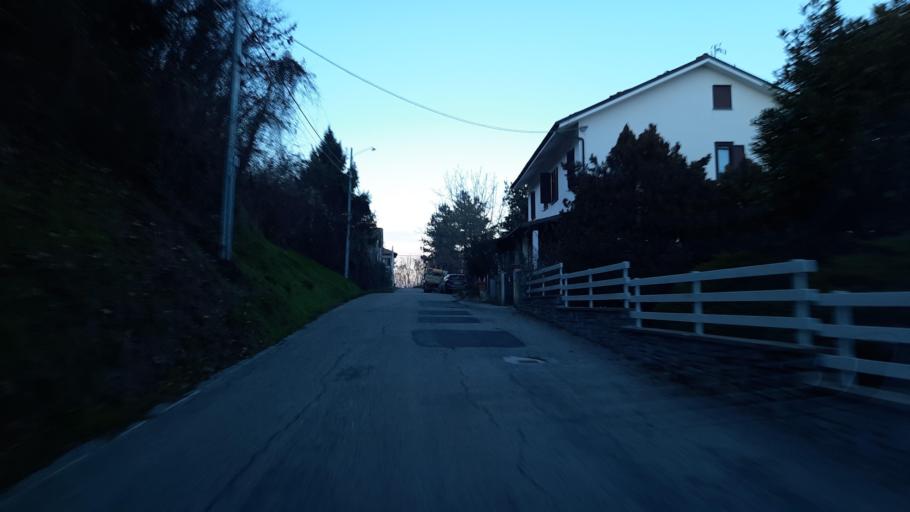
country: IT
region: Piedmont
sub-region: Provincia di Alessandria
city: Camino
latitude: 45.1629
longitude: 8.2870
